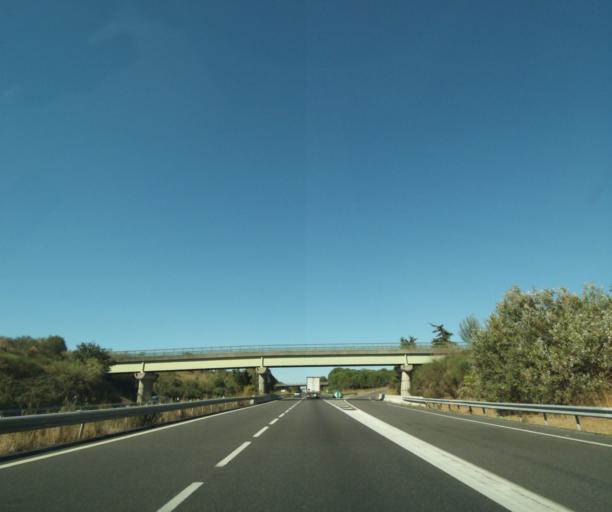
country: FR
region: Languedoc-Roussillon
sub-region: Departement du Gard
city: Garons
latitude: 43.7564
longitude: 4.4284
